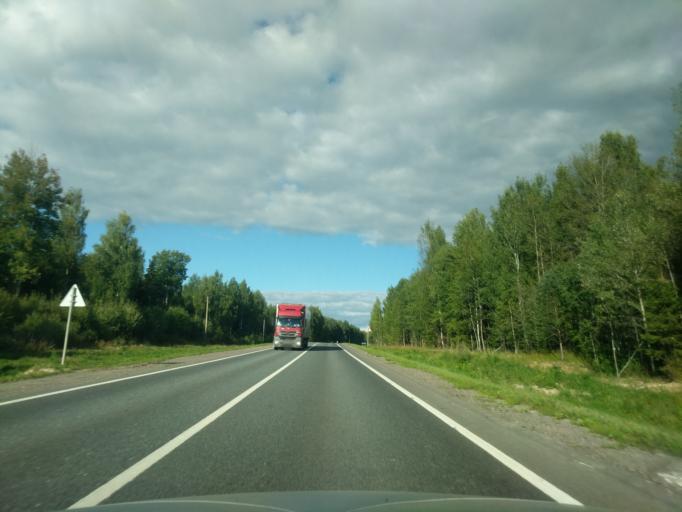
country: RU
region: Kostroma
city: Manturovo
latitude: 58.1636
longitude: 44.4007
